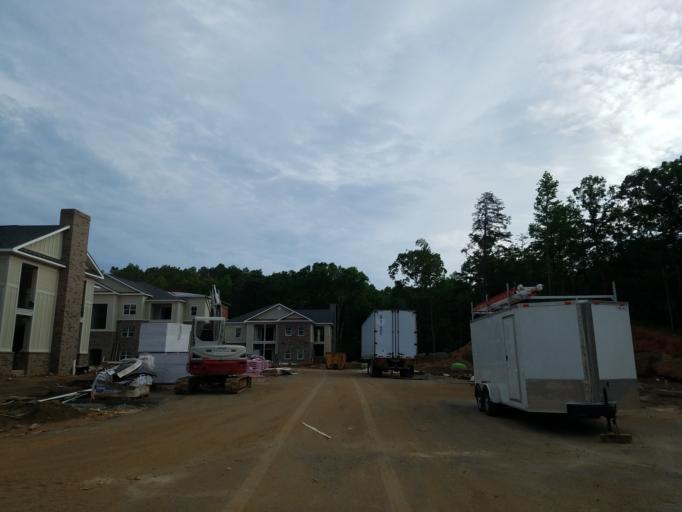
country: US
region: Georgia
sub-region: Lumpkin County
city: Dahlonega
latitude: 34.5162
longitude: -83.9777
